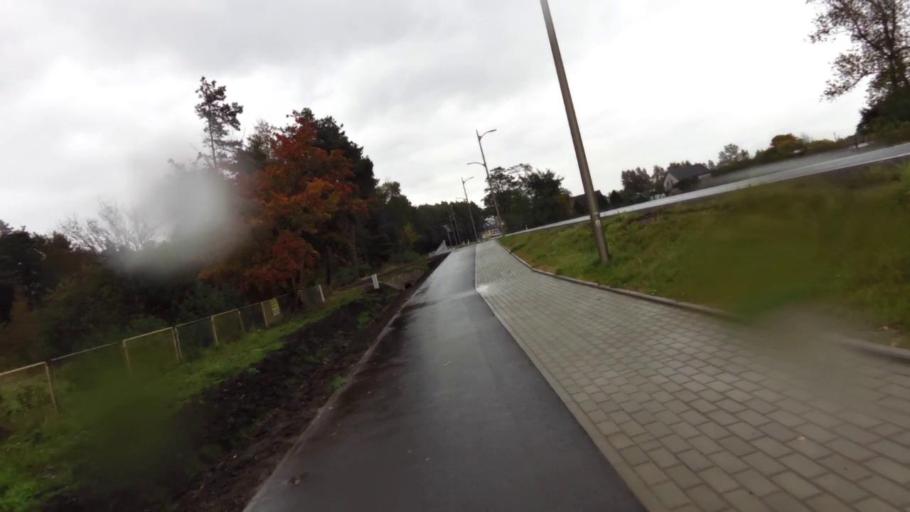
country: PL
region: West Pomeranian Voivodeship
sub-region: Powiat slawienski
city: Darlowo
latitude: 54.3914
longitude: 16.3385
